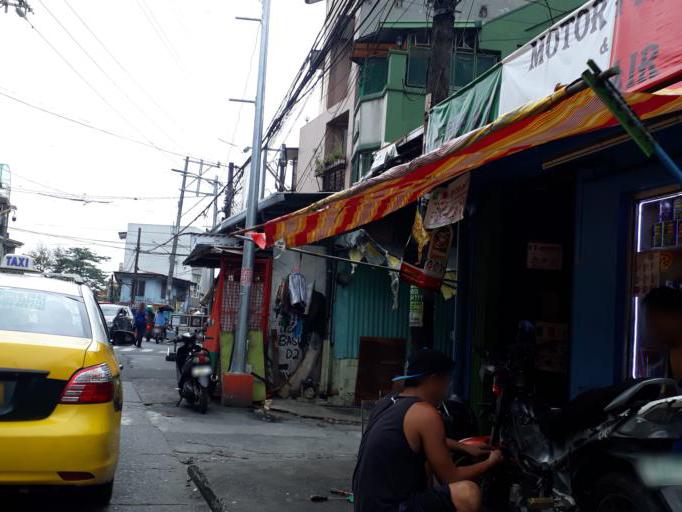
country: PH
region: Metro Manila
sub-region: City of Manila
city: Manila
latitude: 14.6360
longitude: 120.9799
